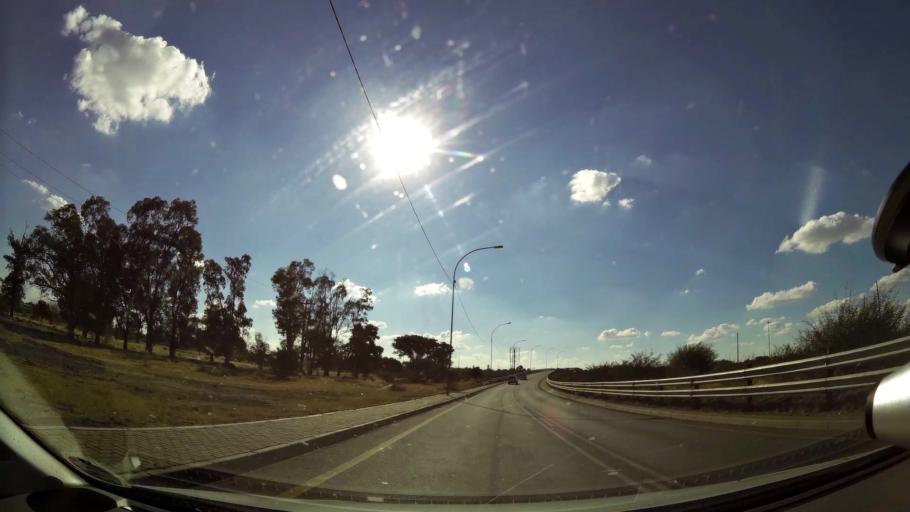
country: ZA
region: Northern Cape
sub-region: Frances Baard District Municipality
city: Kimberley
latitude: -28.7771
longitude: 24.7653
